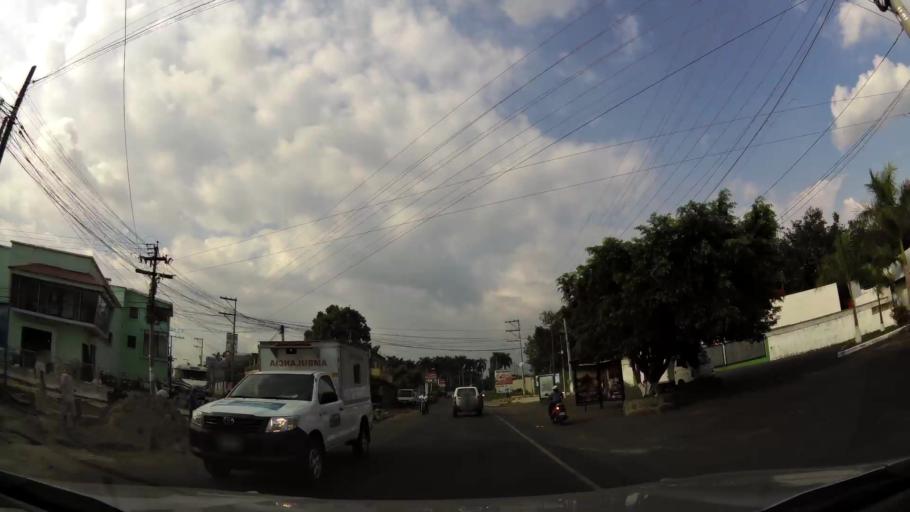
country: GT
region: Retalhuleu
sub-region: Municipio de Retalhuleu
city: Retalhuleu
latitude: 14.5375
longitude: -91.6724
